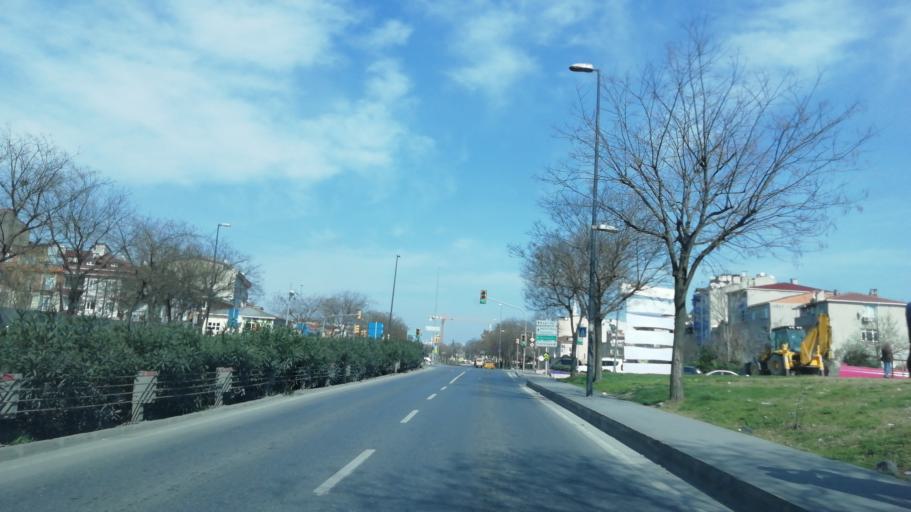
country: TR
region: Istanbul
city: Bagcilar
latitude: 41.0208
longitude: 28.8486
